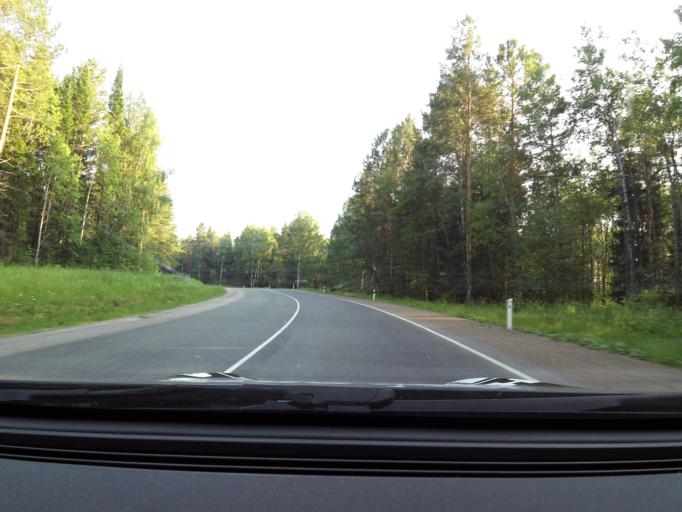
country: RU
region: Sverdlovsk
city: Nizhniye Sergi
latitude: 56.5798
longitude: 59.2131
